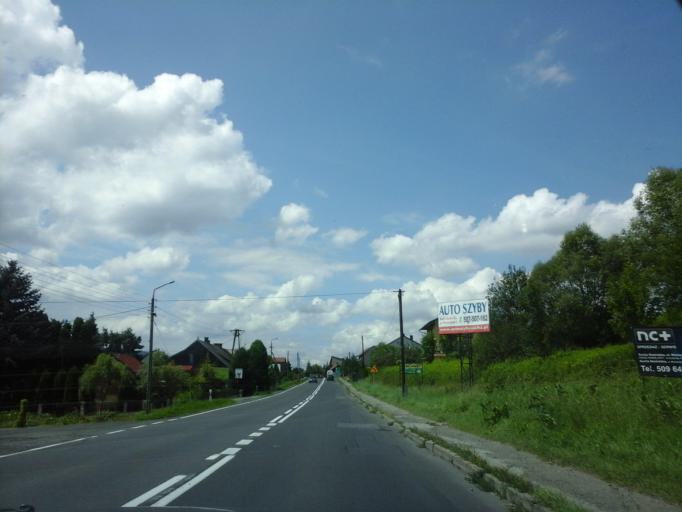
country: PL
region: Lesser Poland Voivodeship
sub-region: Powiat suski
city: Grzechynia
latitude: 49.7335
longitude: 19.6479
